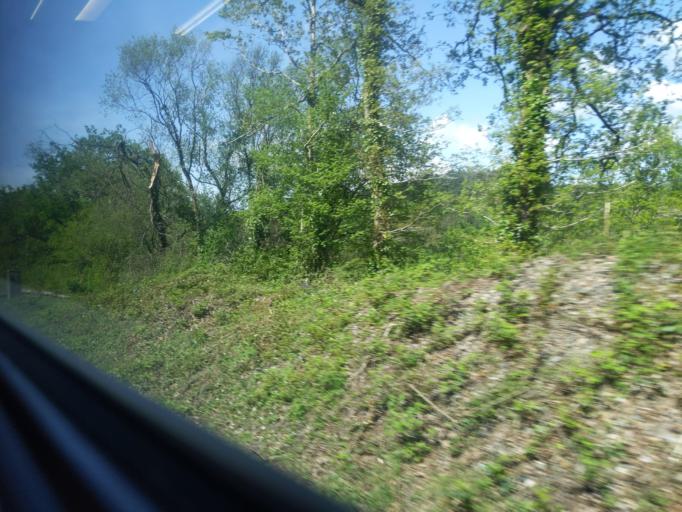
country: GB
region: England
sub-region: Cornwall
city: Lostwithiel
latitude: 50.4529
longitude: -4.5799
